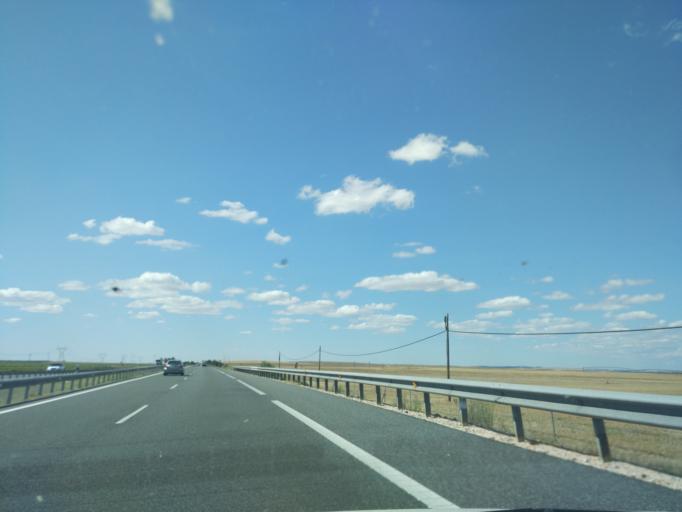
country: ES
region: Castille and Leon
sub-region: Provincia de Valladolid
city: Ataquines
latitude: 41.1907
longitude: -4.8126
